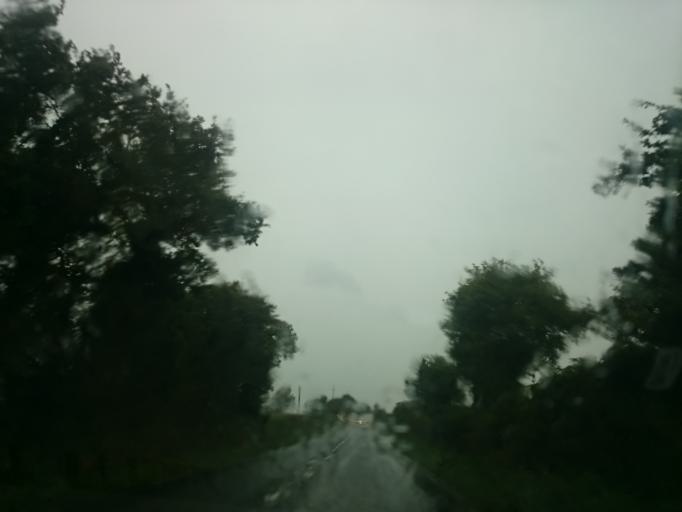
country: FR
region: Brittany
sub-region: Departement du Finistere
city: Gouesnou
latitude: 48.4722
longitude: -4.4419
